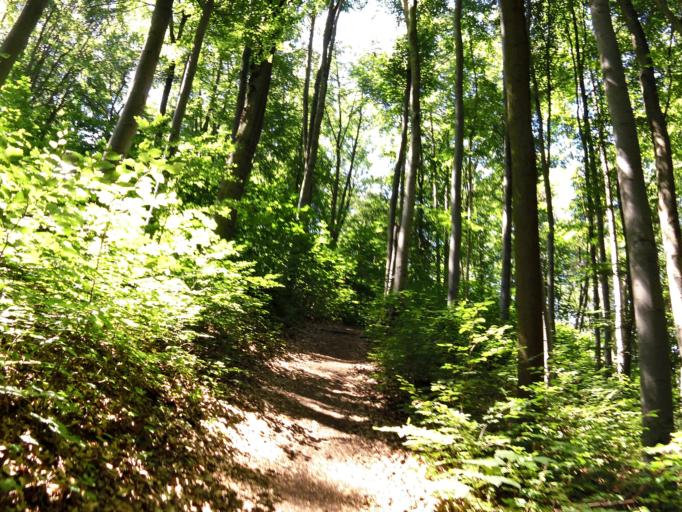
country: DE
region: Thuringia
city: Seebach
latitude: 50.9572
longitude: 10.4560
